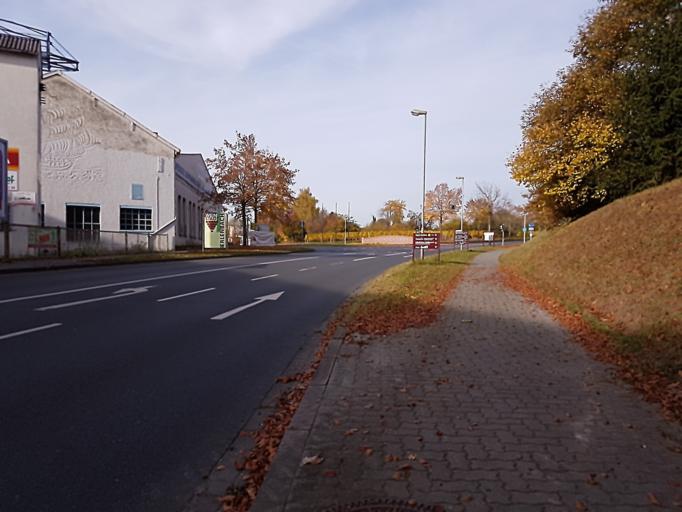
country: DE
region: Bavaria
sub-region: Regierungsbezirk Unterfranken
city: Erlenbach am Main
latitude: 49.7979
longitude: 9.1641
